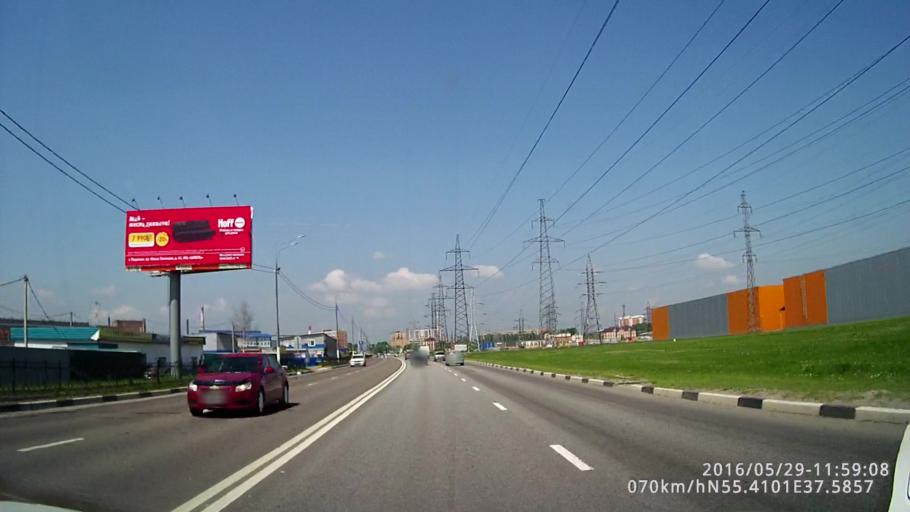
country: RU
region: Moskovskaya
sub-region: Podol'skiy Rayon
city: Podol'sk
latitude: 55.4105
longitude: 37.5852
